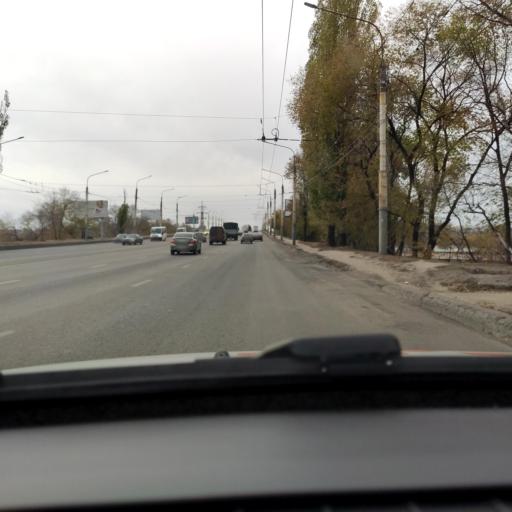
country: RU
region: Voronezj
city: Voronezh
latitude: 51.6327
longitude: 39.2283
